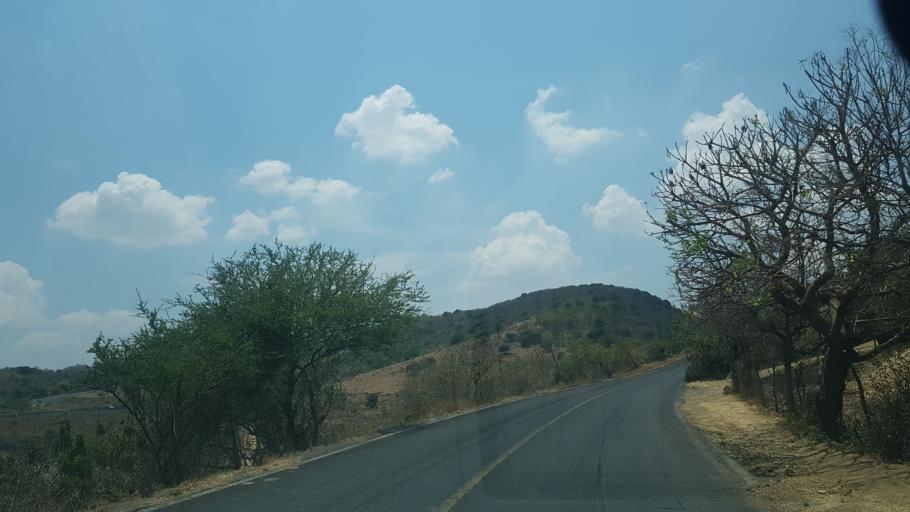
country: MX
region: Puebla
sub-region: Atzitzihuacan
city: Santiago Atzitzihuacan
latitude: 18.8339
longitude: -98.5975
